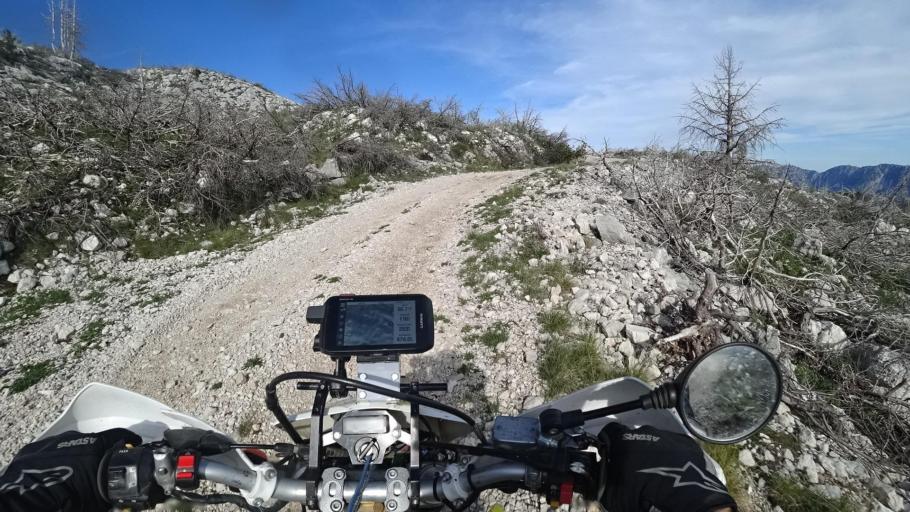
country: BA
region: Federation of Bosnia and Herzegovina
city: Kocerin
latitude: 43.5791
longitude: 17.5426
